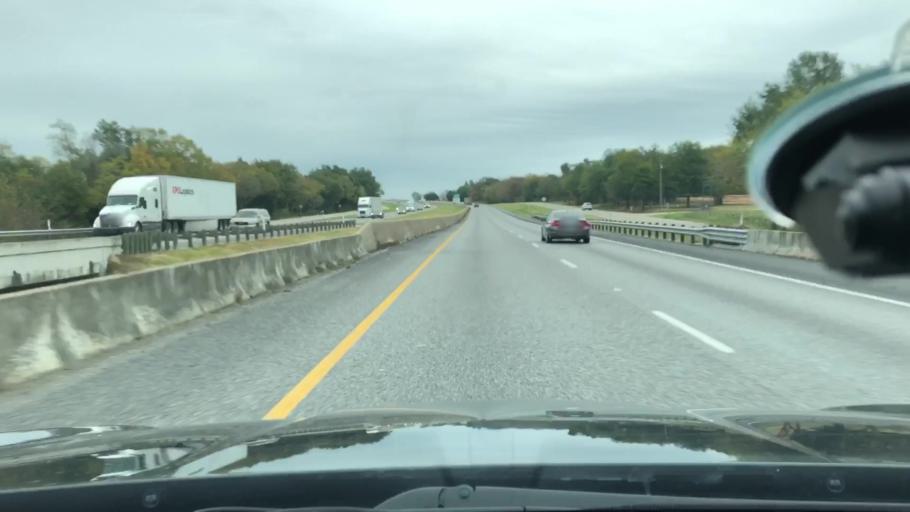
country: US
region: Texas
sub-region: Hunt County
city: Greenville
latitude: 33.1289
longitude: -95.9776
